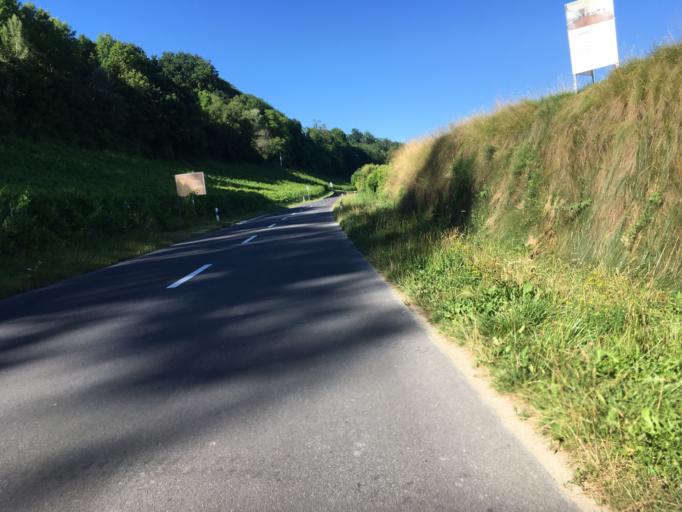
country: CH
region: Fribourg
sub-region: See District
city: Bas-Vully
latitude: 46.9404
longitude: 7.0608
